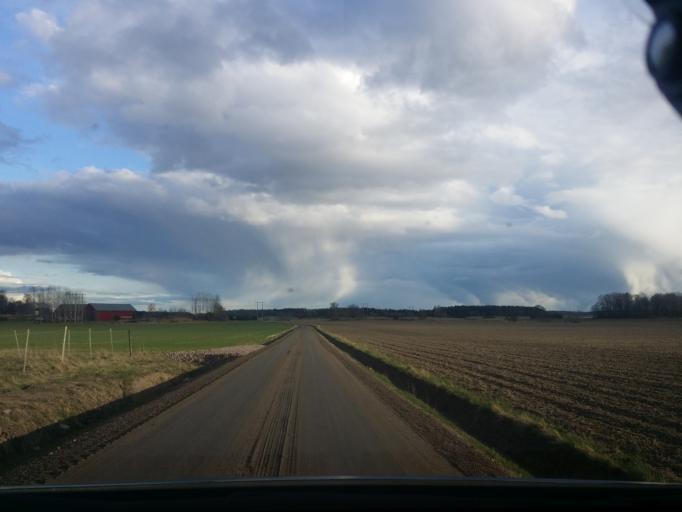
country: SE
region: Vaestmanland
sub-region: Vasteras
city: Vasteras
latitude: 59.5556
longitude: 16.4498
